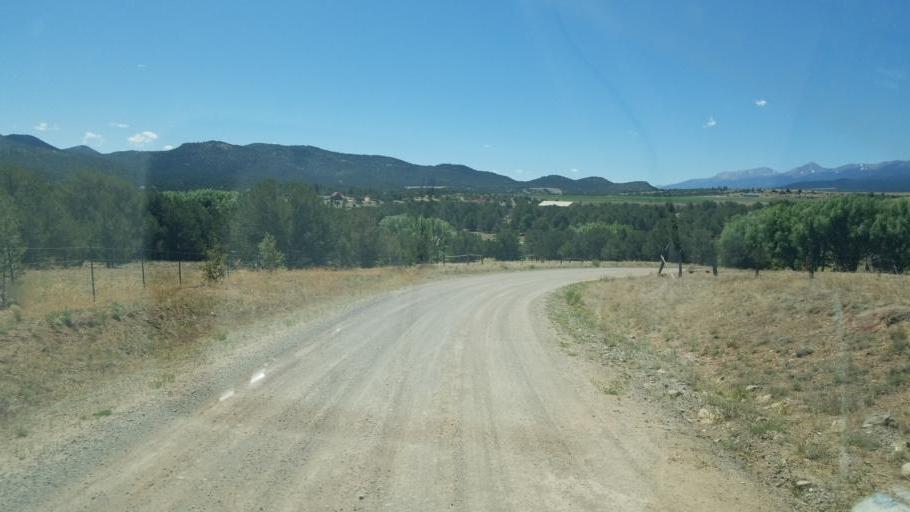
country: US
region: Colorado
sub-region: Custer County
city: Westcliffe
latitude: 38.3046
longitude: -105.6149
